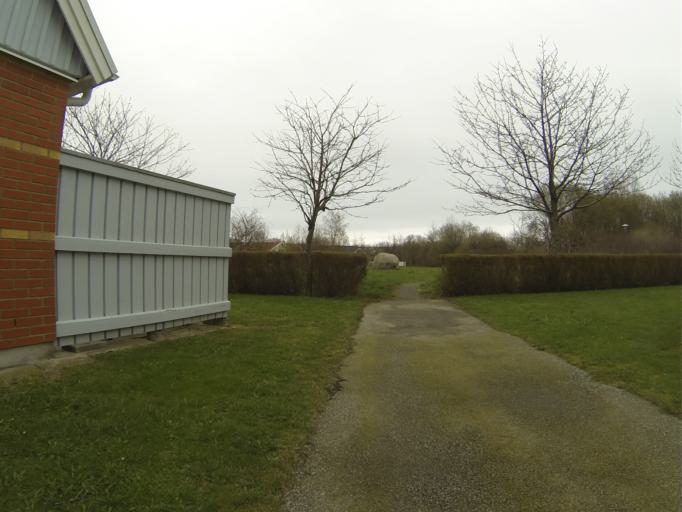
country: SE
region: Skane
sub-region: Simrishamns Kommun
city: Simrishamn
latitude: 55.5436
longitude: 14.3417
